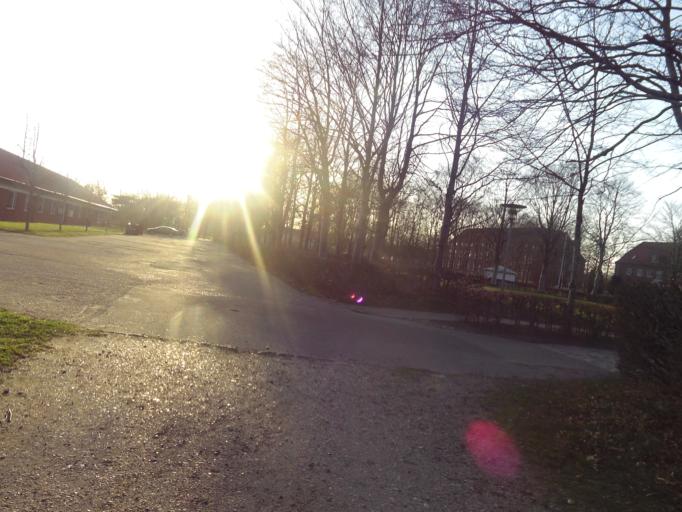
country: DK
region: South Denmark
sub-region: Esbjerg Kommune
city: Ribe
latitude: 55.3246
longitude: 8.7761
